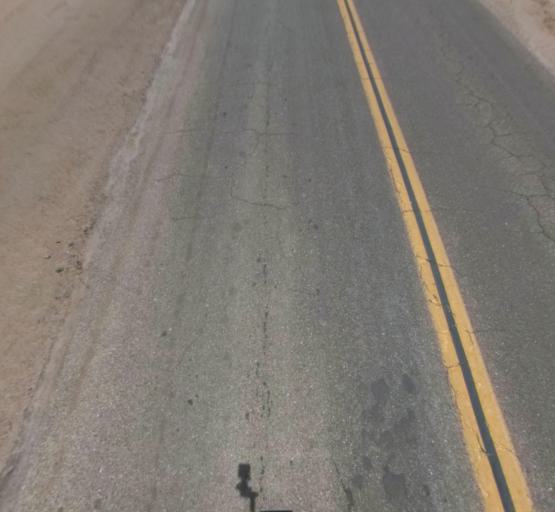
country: US
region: California
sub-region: Madera County
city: Parkwood
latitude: 36.8733
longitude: -120.0922
